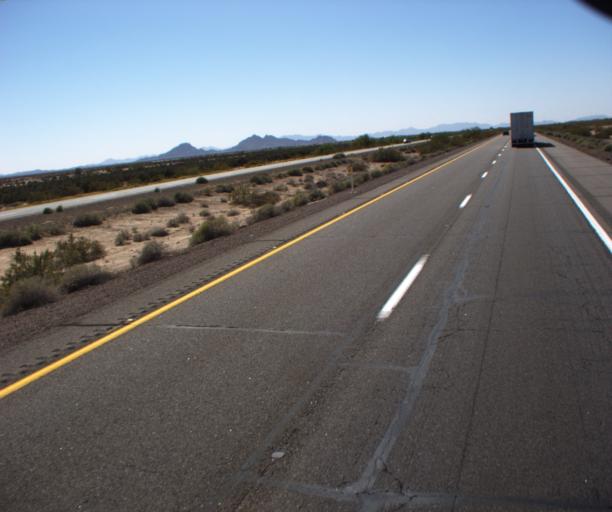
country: US
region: Arizona
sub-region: Yuma County
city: Wellton
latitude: 32.7026
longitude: -113.8947
